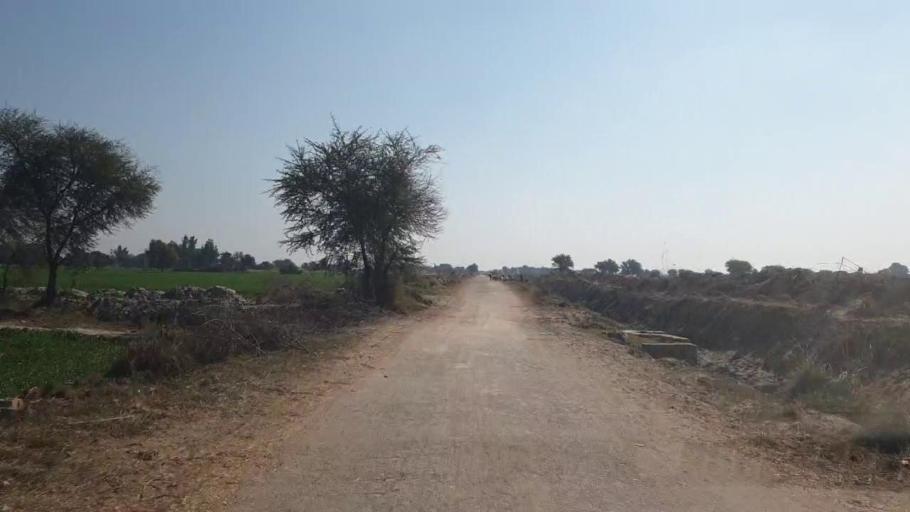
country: PK
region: Sindh
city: Shahdadpur
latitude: 25.9614
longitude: 68.6224
